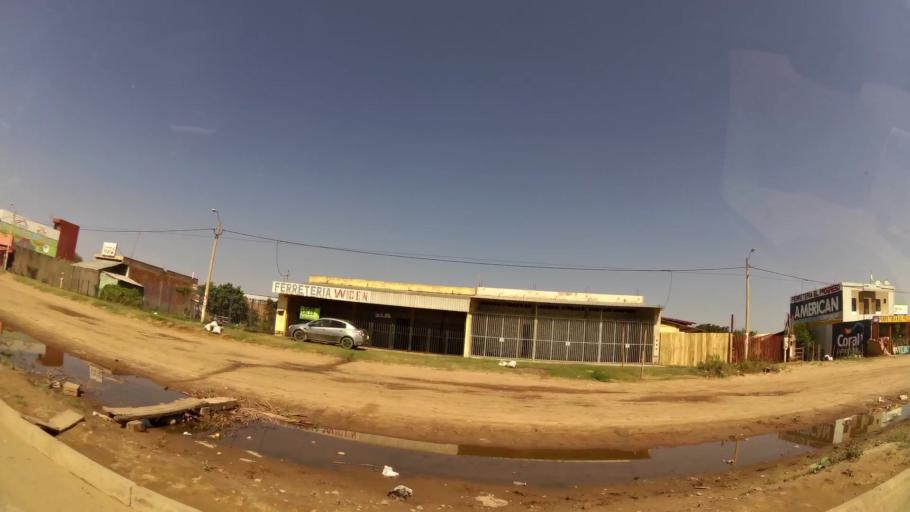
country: BO
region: Santa Cruz
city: Cotoca
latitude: -17.7281
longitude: -63.0894
